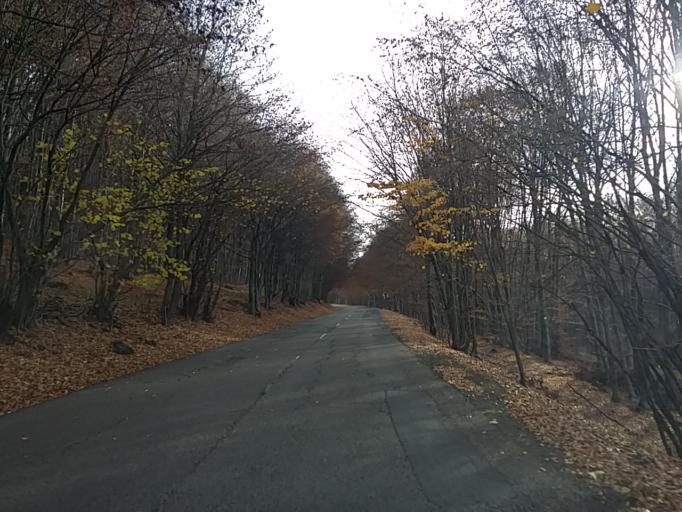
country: HU
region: Heves
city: Paradsasvar
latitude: 47.8700
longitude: 19.9980
